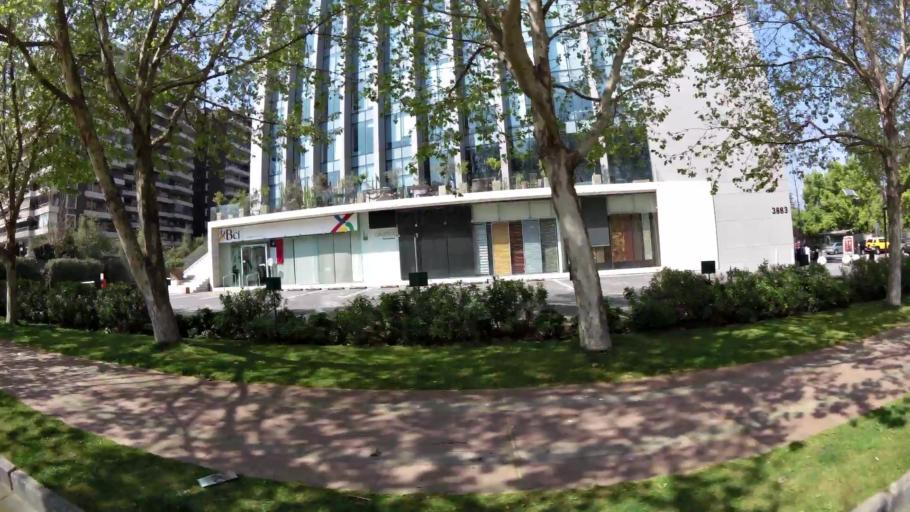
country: CL
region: Santiago Metropolitan
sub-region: Provincia de Santiago
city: Villa Presidente Frei, Nunoa, Santiago, Chile
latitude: -33.3981
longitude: -70.6008
